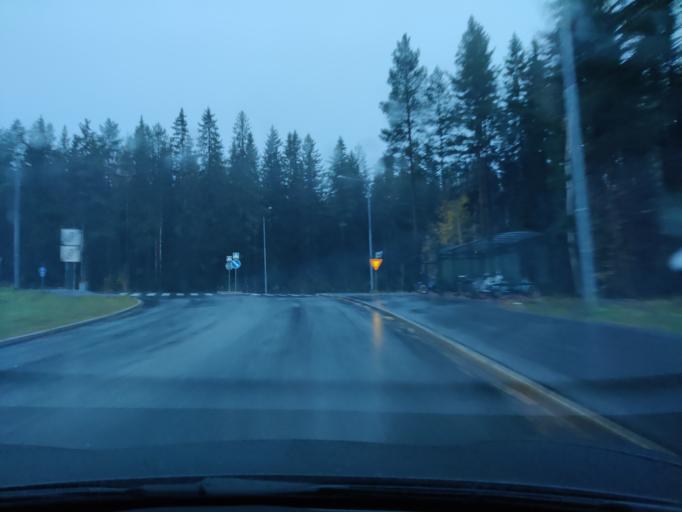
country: FI
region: Northern Savo
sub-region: Kuopio
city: Kuopio
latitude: 62.8325
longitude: 27.7132
